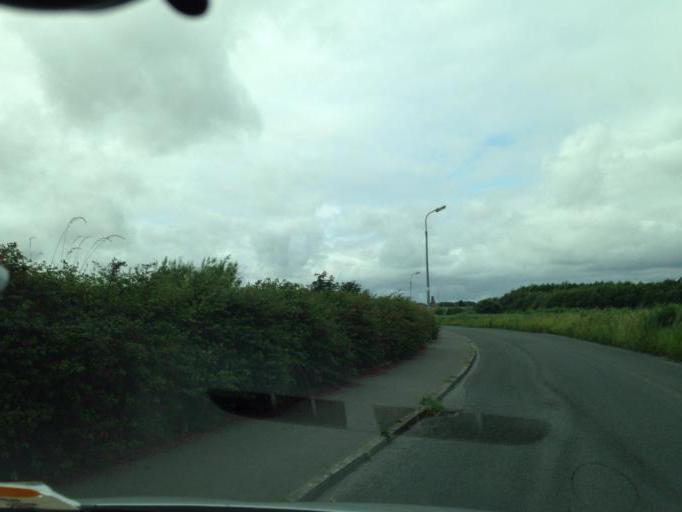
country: IE
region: Connaught
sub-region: County Galway
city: Gaillimh
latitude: 53.2811
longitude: -9.0535
